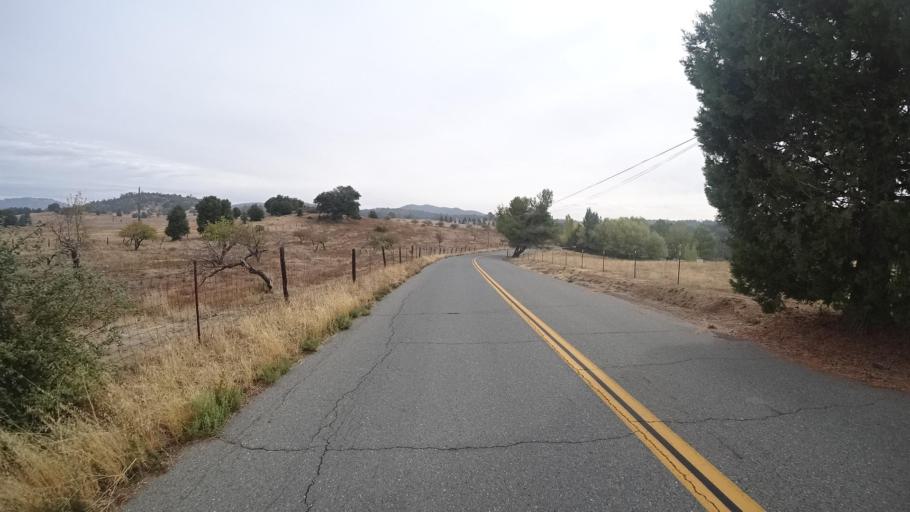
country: US
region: California
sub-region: San Diego County
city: Julian
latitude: 33.0481
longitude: -116.6162
